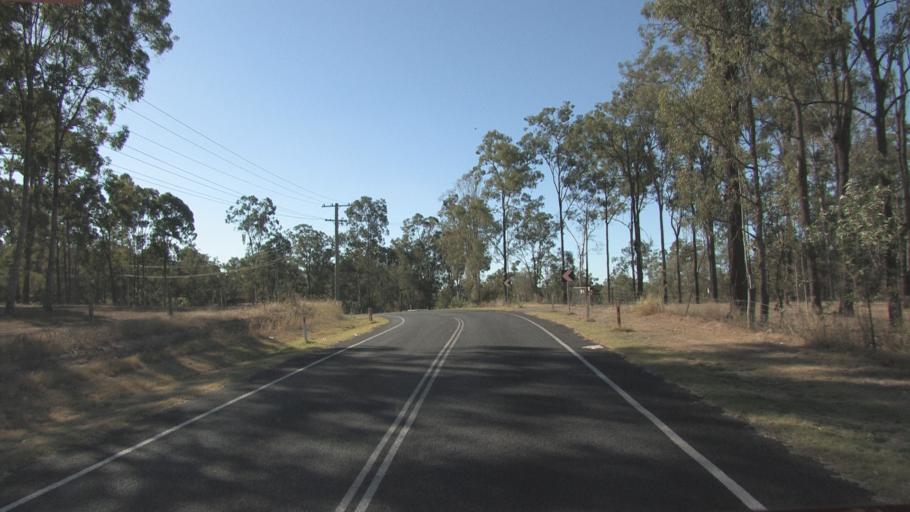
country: AU
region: Queensland
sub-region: Logan
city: North Maclean
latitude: -27.8052
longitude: 153.0342
